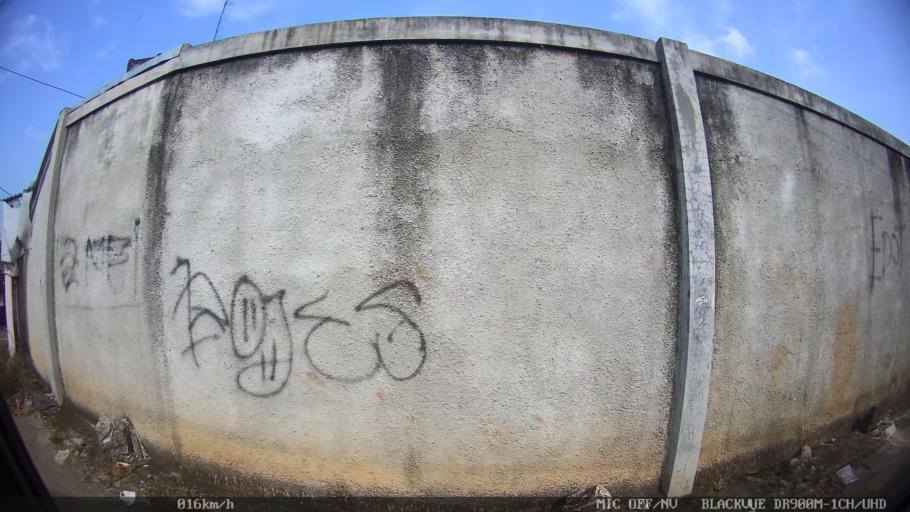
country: ID
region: Lampung
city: Kedaton
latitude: -5.3915
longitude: 105.2221
